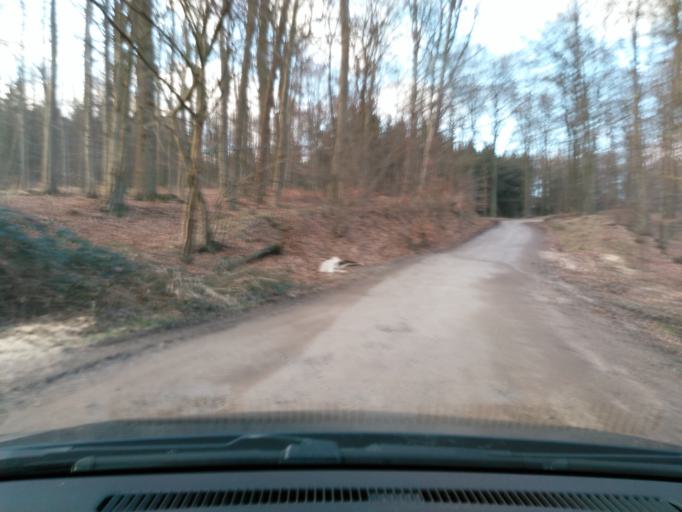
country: DE
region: Schleswig-Holstein
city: Klausdorf
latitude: 54.2697
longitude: 10.2026
